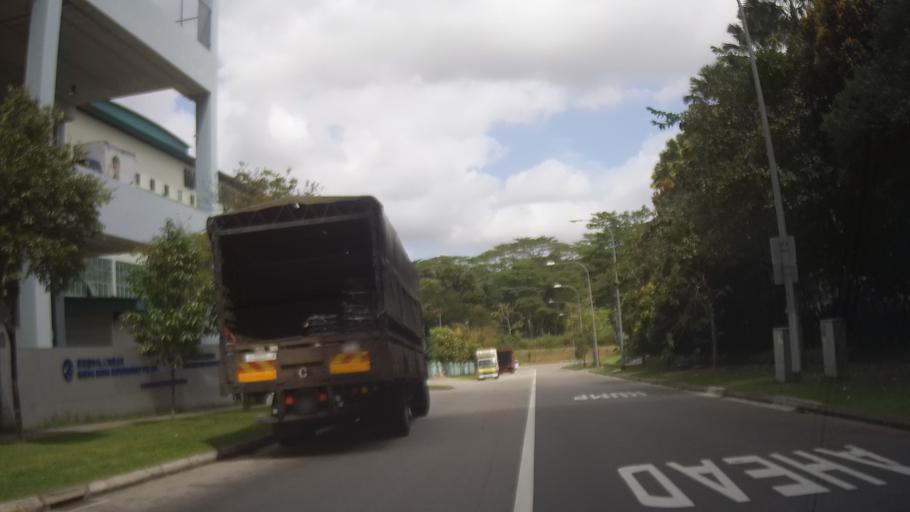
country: MY
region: Johor
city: Johor Bahru
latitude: 1.4100
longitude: 103.7578
